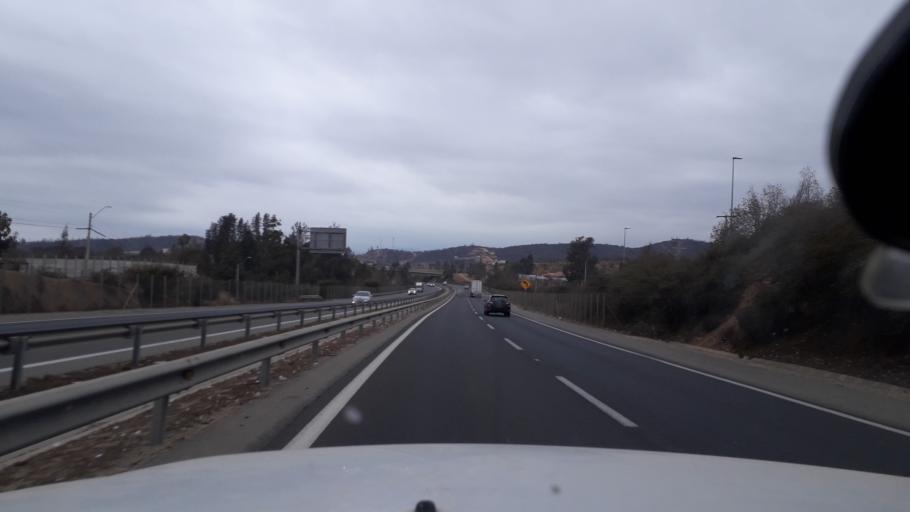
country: CL
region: Valparaiso
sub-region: Provincia de Marga Marga
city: Villa Alemana
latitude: -33.0632
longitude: -71.3478
